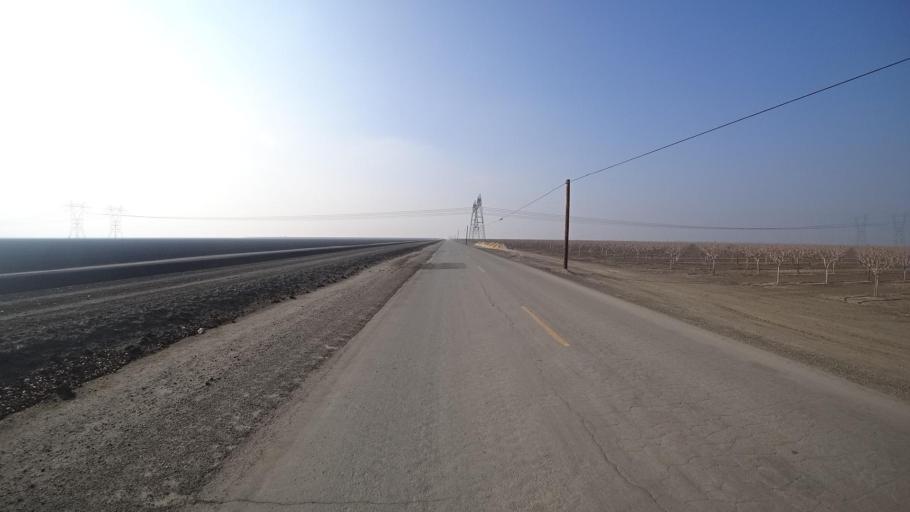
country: US
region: California
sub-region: Kern County
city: Greenfield
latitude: 35.1514
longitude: -119.0437
